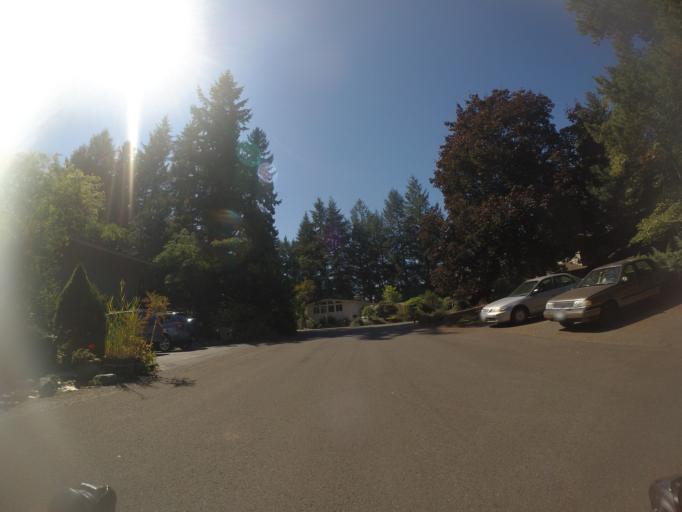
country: US
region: Washington
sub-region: Pierce County
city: University Place
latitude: 47.2156
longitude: -122.5619
